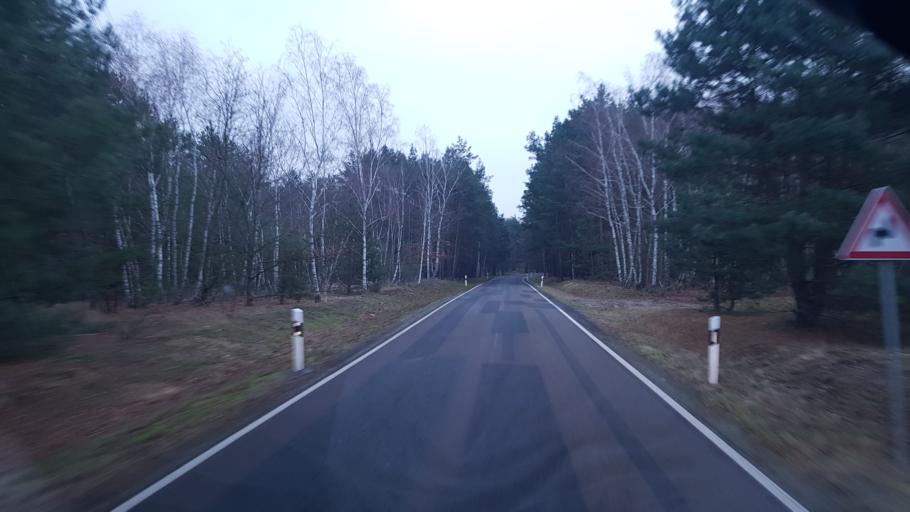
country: DE
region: Brandenburg
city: Guhrow
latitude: 51.8522
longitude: 14.2262
